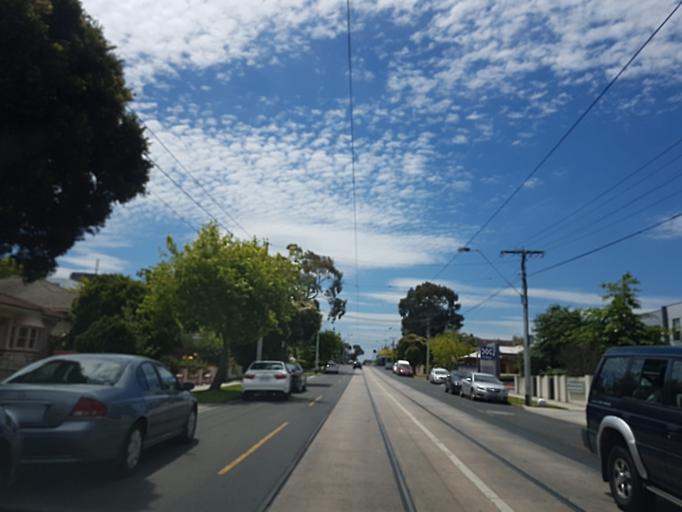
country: AU
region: Victoria
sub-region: Glen Eira
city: Caulfield
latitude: -37.8818
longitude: 145.0229
